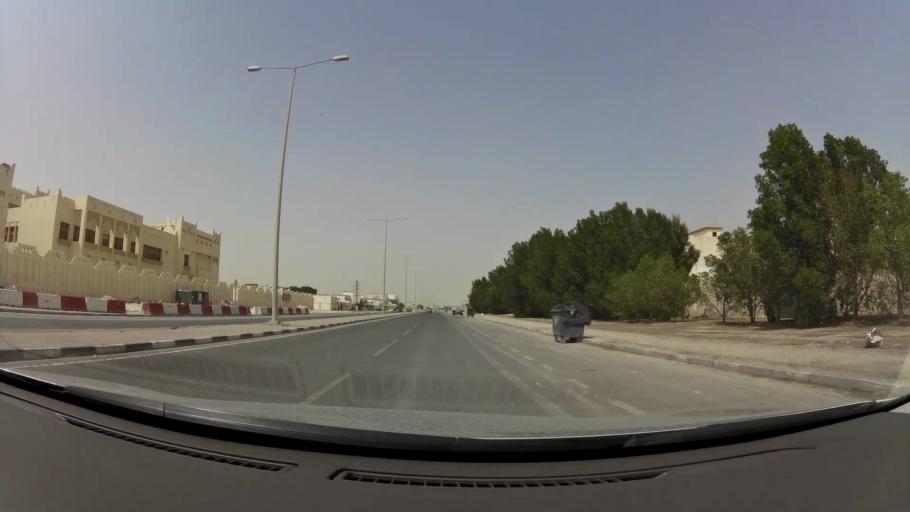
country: QA
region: Baladiyat ar Rayyan
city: Ar Rayyan
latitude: 25.2343
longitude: 51.4204
